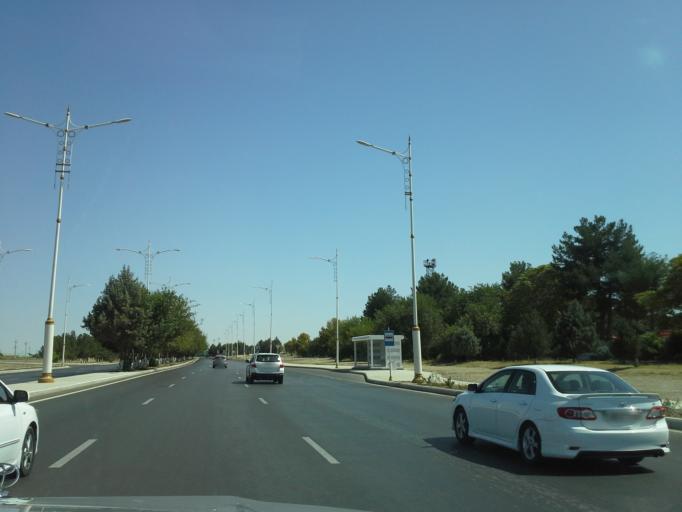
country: TM
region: Ahal
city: Ashgabat
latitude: 37.9224
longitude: 58.4417
